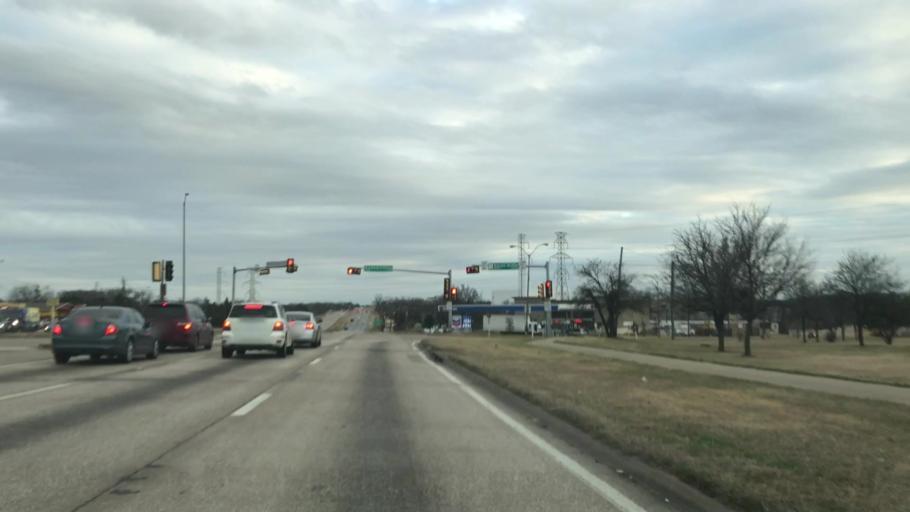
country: US
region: Texas
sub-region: Dallas County
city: Cockrell Hill
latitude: 32.7115
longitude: -96.9091
